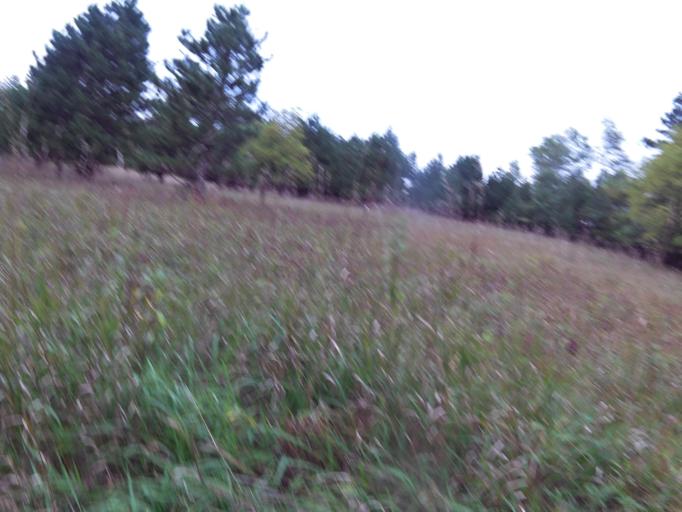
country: US
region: Minnesota
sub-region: Washington County
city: Afton
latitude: 44.8691
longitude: -92.7844
